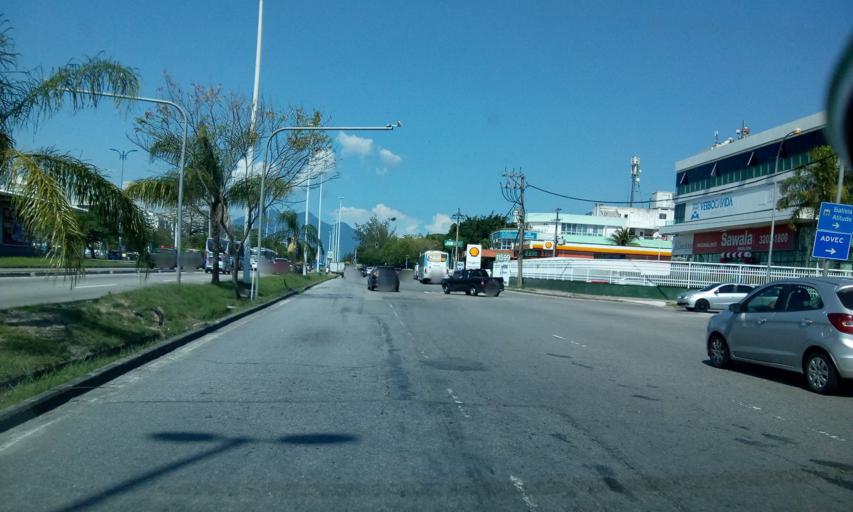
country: BR
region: Rio de Janeiro
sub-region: Nilopolis
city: Nilopolis
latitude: -23.0059
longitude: -43.4323
